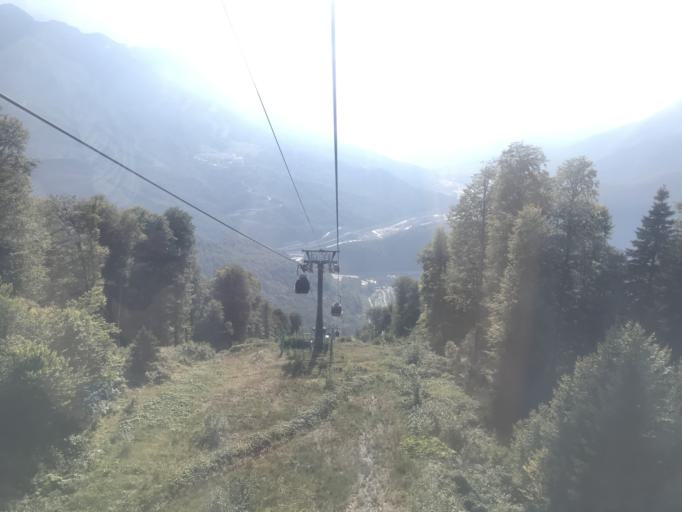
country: RU
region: Krasnodarskiy
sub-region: Sochi City
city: Krasnaya Polyana
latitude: 43.6925
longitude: 40.3099
